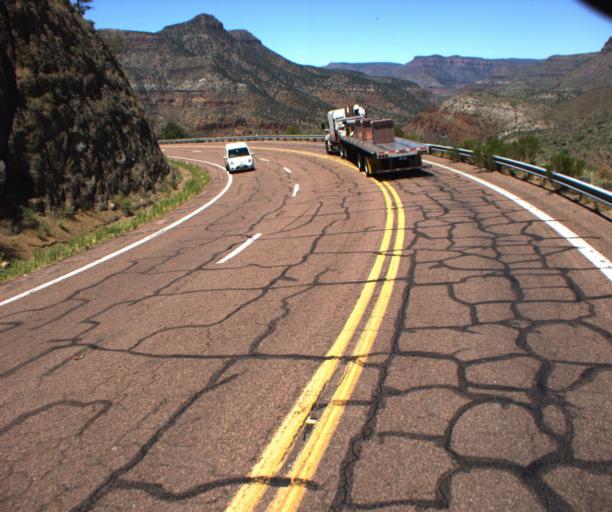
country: US
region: Arizona
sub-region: Navajo County
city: Cibecue
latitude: 33.7941
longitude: -110.4961
